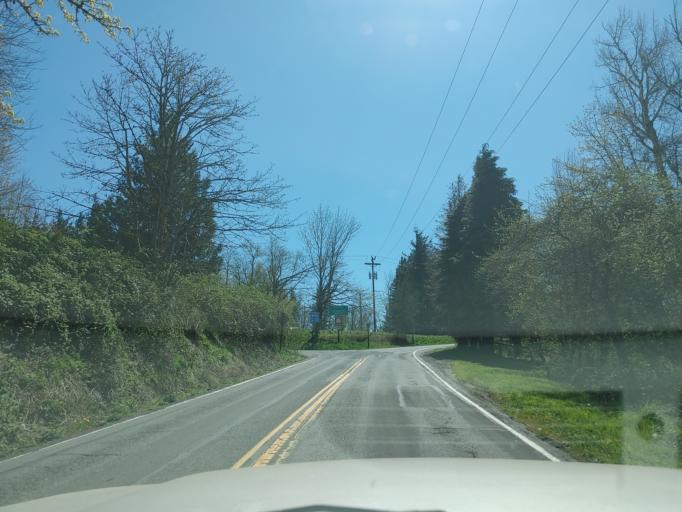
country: US
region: Washington
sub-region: Clark County
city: Washougal
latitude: 45.5329
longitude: -122.2901
